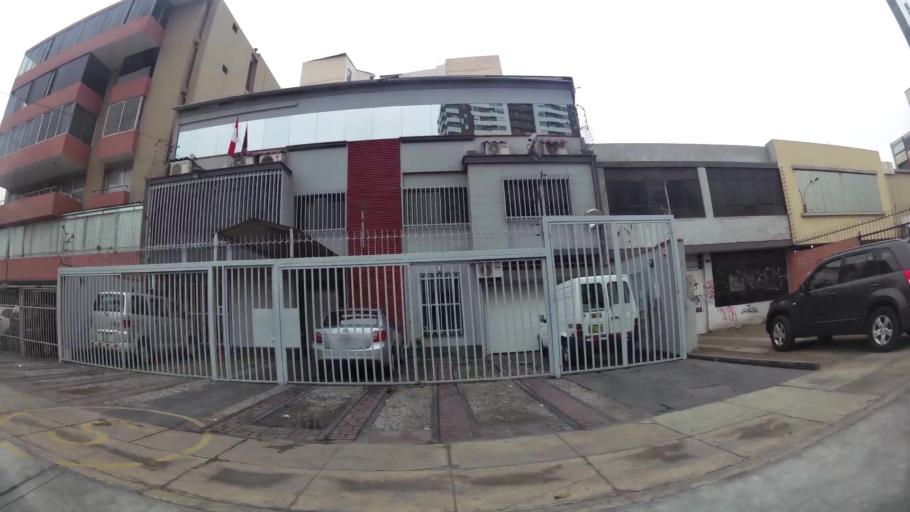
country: PE
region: Lima
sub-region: Lima
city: San Isidro
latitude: -12.1065
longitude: -77.0275
